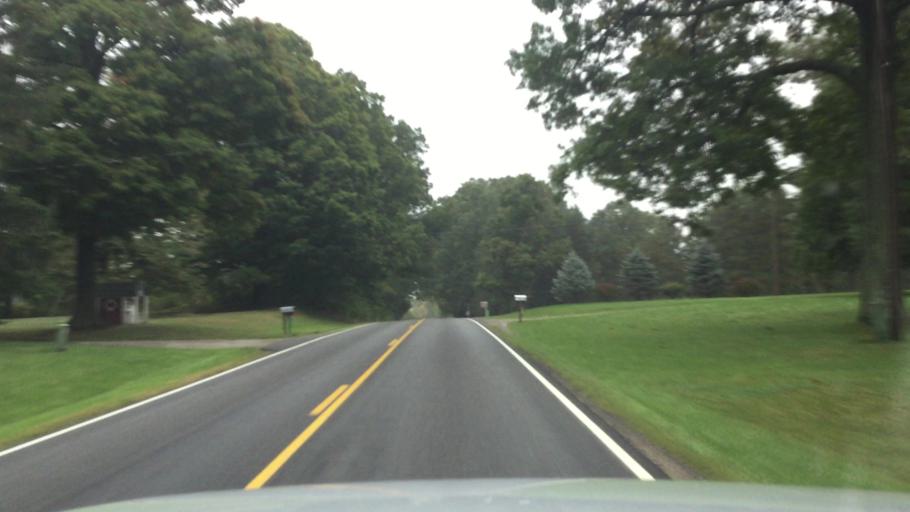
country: US
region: Michigan
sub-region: Shiawassee County
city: Owosso
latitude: 42.9357
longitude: -84.2136
